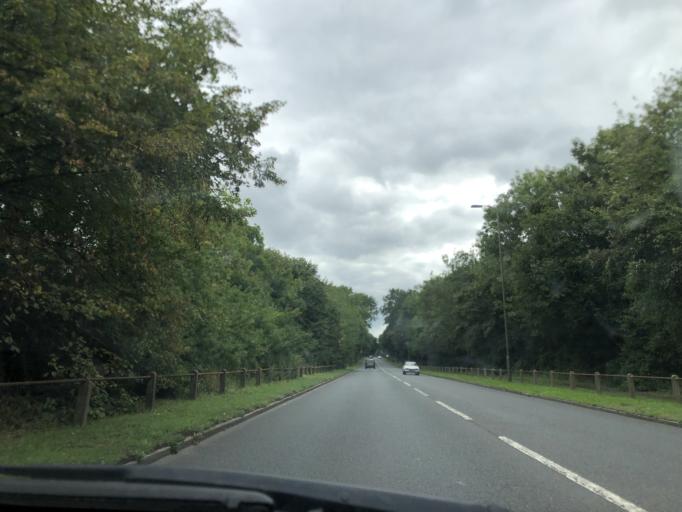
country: GB
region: England
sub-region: Greater London
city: Orpington
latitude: 51.3615
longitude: 0.1168
